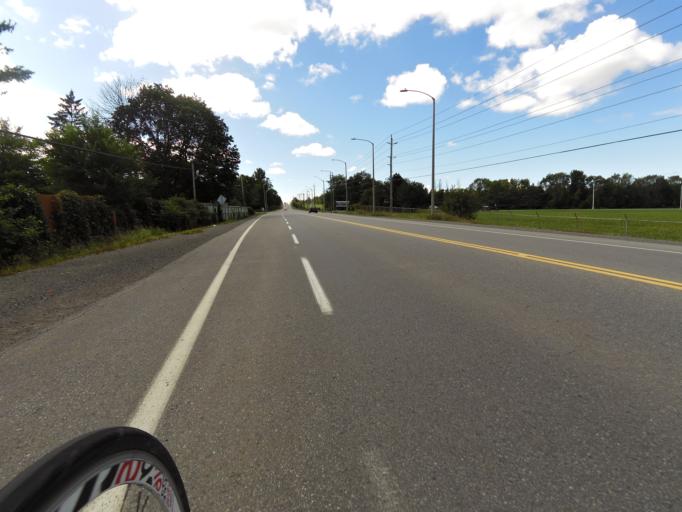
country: CA
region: Ontario
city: Bells Corners
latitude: 45.2843
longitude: -75.7658
